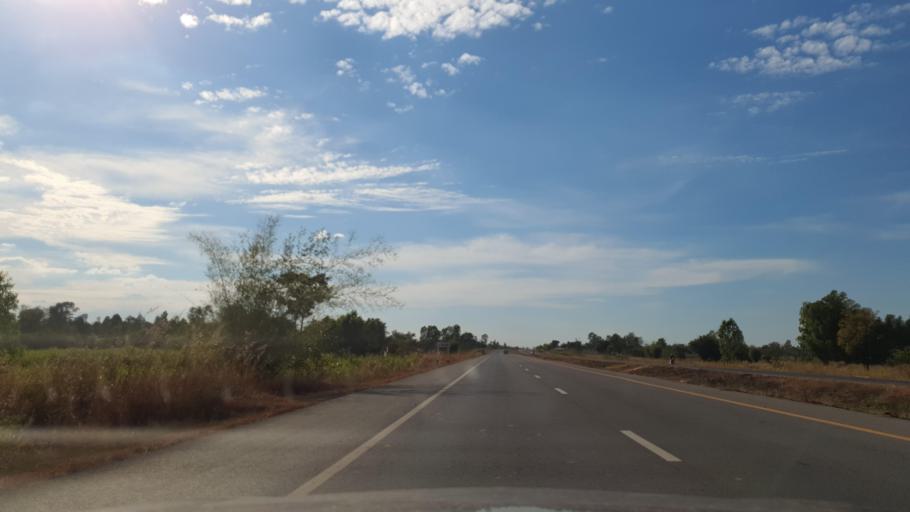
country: TH
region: Kalasin
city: Don Chan
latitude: 16.4113
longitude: 103.7516
